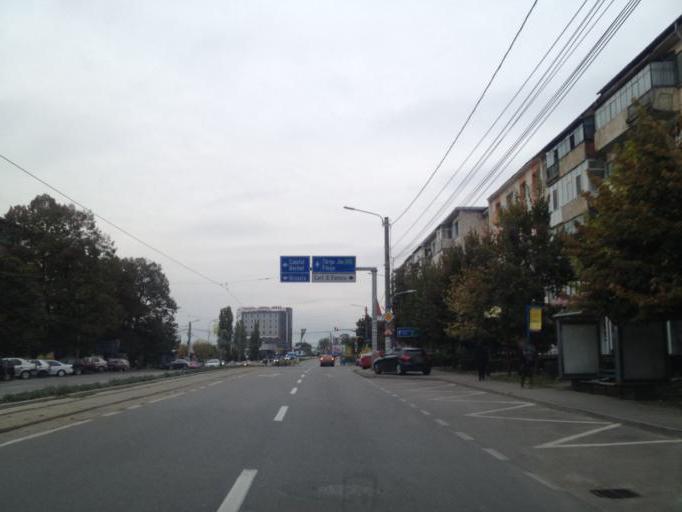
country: RO
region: Dolj
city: Craiova
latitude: 44.3271
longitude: 23.7812
